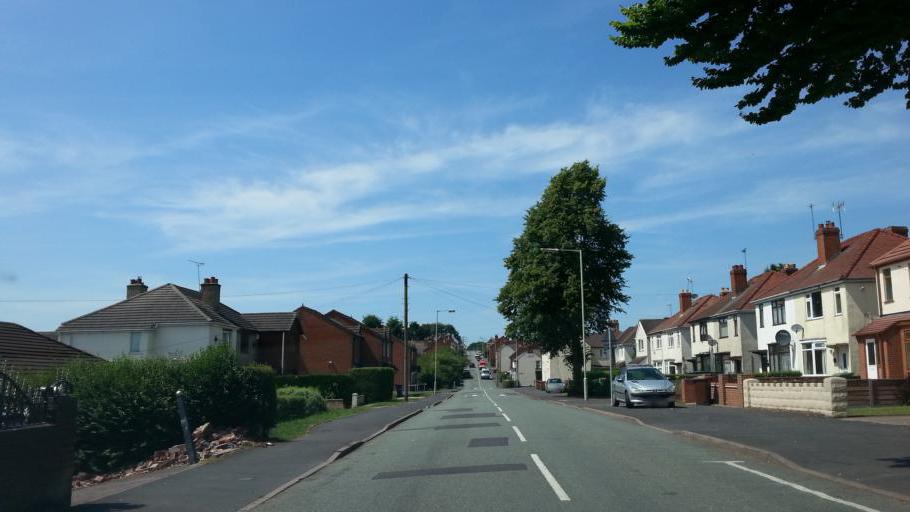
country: GB
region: England
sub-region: Staffordshire
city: Cannock
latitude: 52.7106
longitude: -2.0180
